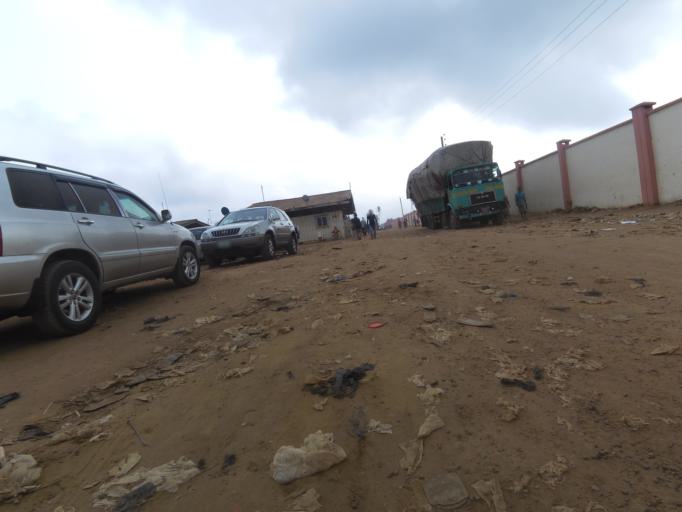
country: BJ
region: Queme
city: Porto-Novo
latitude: 6.3809
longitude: 2.7047
